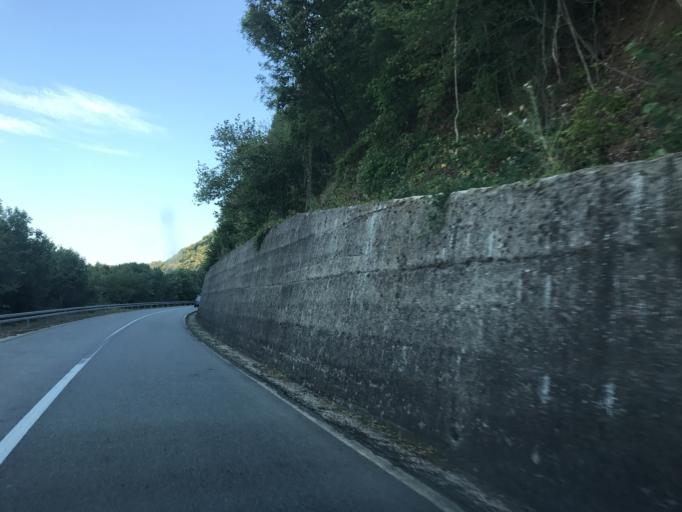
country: RO
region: Mehedinti
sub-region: Comuna Svinita
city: Svinita
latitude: 44.4912
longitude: 22.0713
